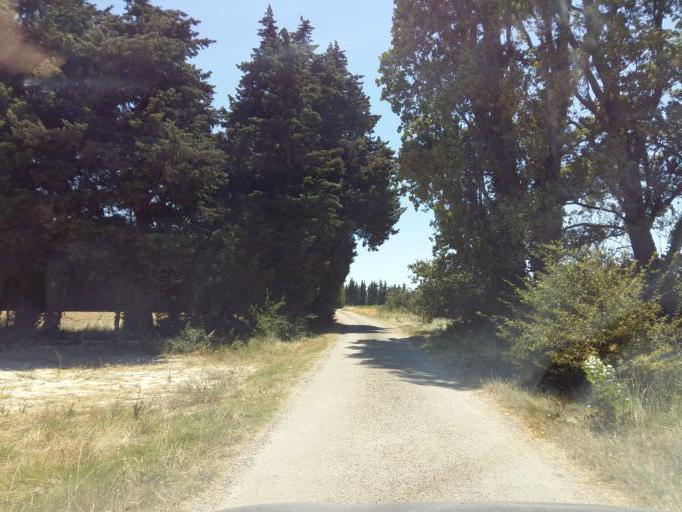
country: FR
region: Provence-Alpes-Cote d'Azur
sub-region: Departement du Vaucluse
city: Orange
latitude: 44.1561
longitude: 4.7875
